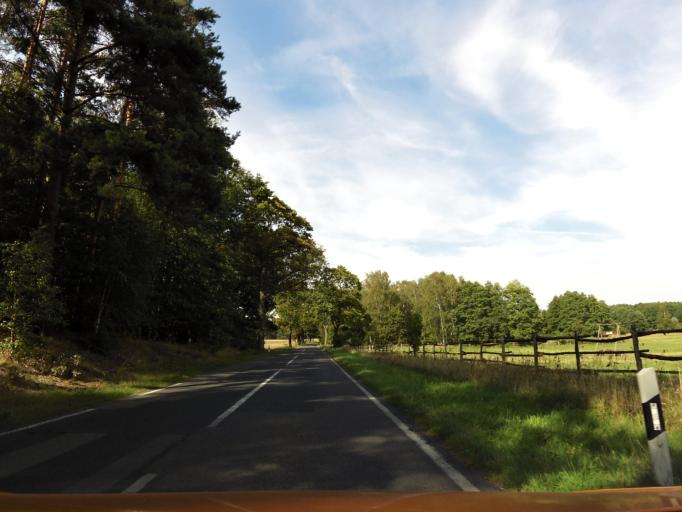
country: DE
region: Brandenburg
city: Michendorf
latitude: 52.2799
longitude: 13.1147
